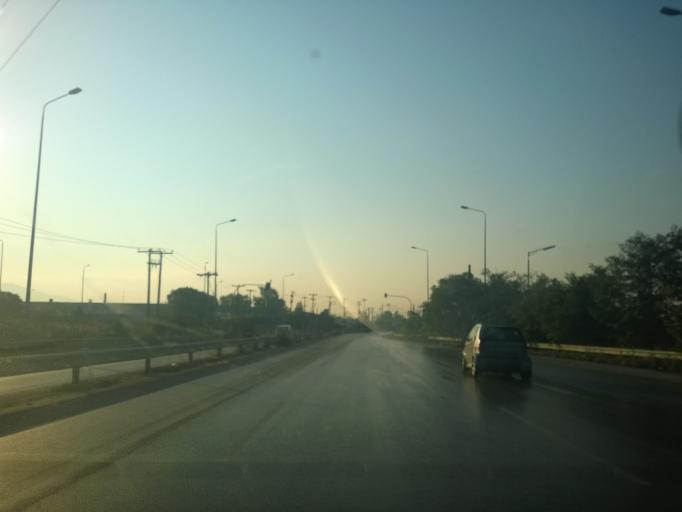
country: GR
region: Central Macedonia
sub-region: Nomos Thessalonikis
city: Menemeni
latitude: 40.6520
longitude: 22.9009
